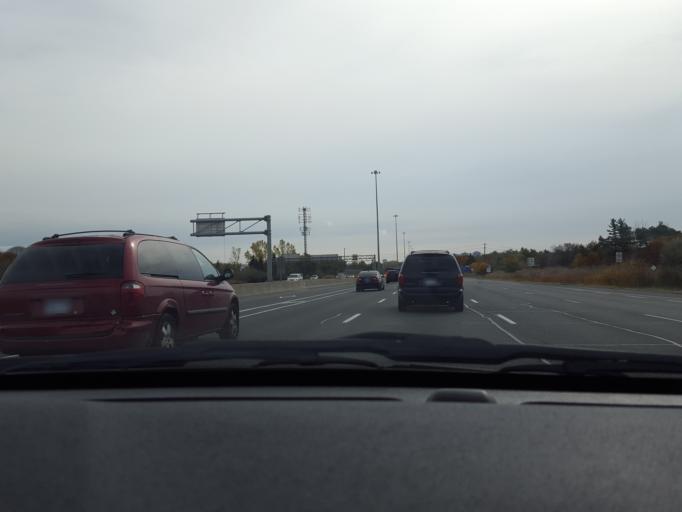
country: CA
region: Ontario
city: Willowdale
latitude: 43.8317
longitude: -79.3656
